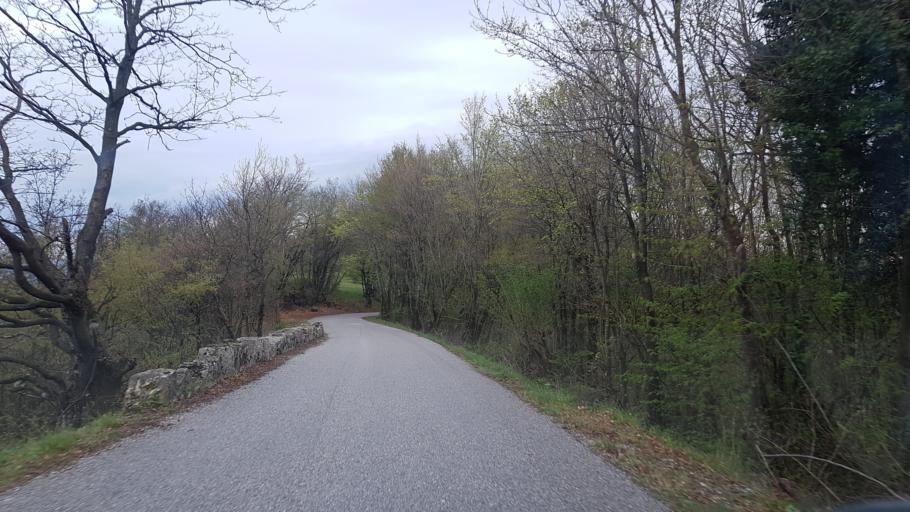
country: SI
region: Kanal
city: Deskle
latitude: 46.0542
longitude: 13.5665
